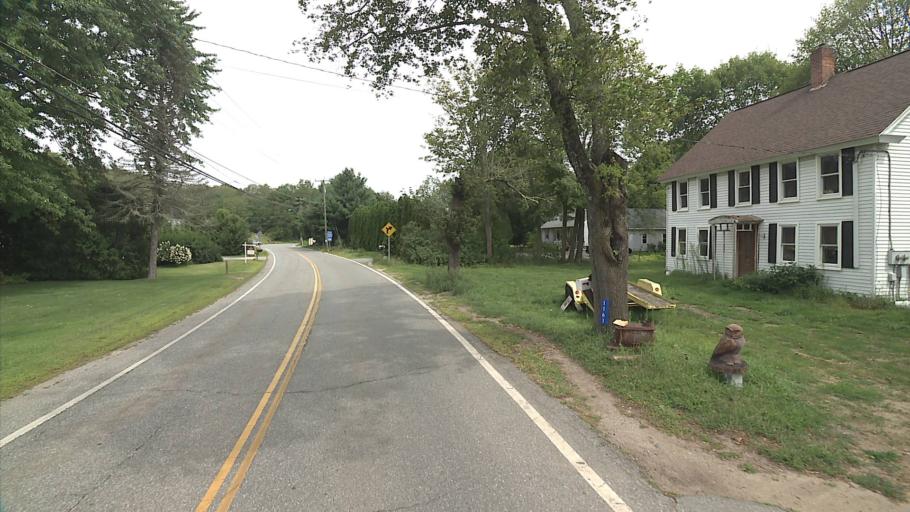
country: US
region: Connecticut
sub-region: Windham County
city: Thompson
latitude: 42.0075
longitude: -71.8451
